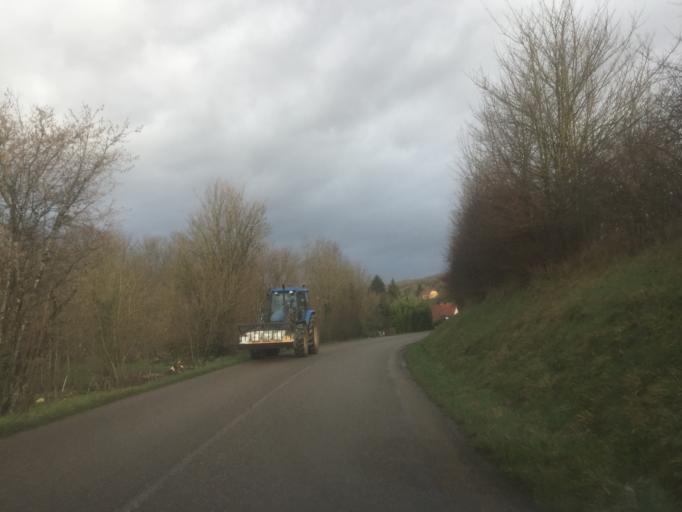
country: FR
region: Franche-Comte
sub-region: Departement du Jura
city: Orchamps
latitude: 47.2206
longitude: 5.6795
